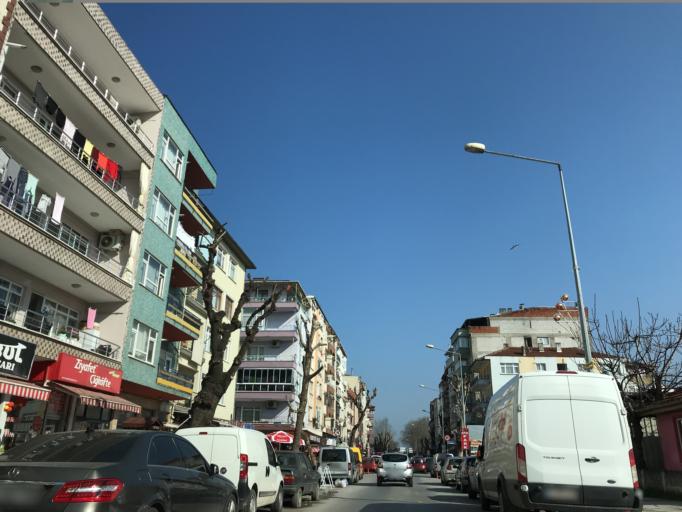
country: TR
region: Yalova
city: Yalova
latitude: 40.6565
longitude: 29.2795
